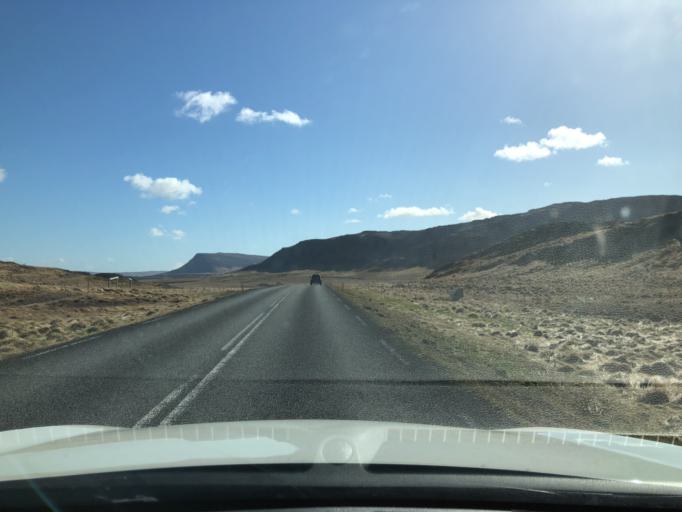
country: IS
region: West
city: Borgarnes
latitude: 64.5712
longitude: -21.6694
